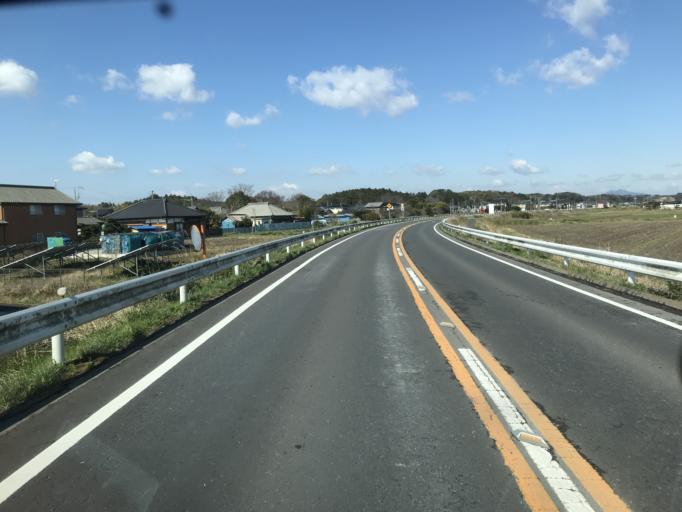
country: JP
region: Ibaraki
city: Inashiki
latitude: 36.0876
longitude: 140.3890
